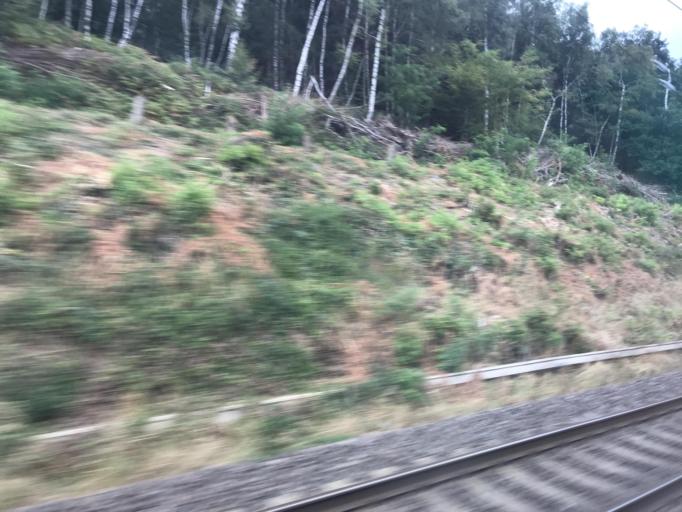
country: DE
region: North Rhine-Westphalia
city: Stolberg
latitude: 50.7970
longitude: 6.2233
